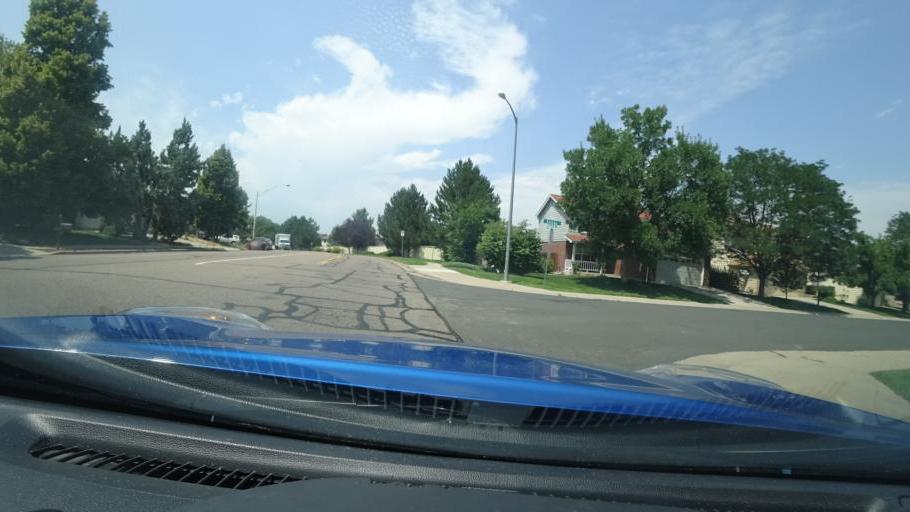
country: US
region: Colorado
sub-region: Adams County
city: Aurora
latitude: 39.6649
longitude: -104.7683
